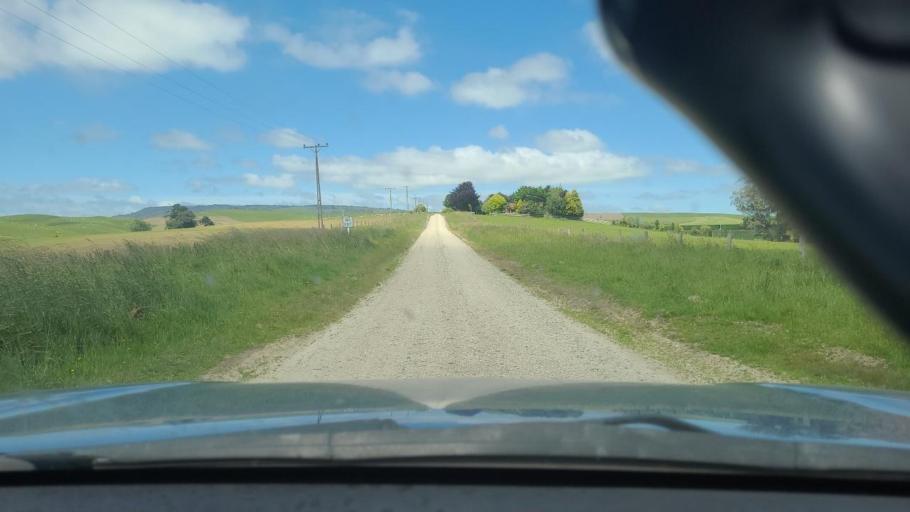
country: NZ
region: Southland
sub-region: Gore District
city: Gore
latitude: -46.3597
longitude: 168.9470
